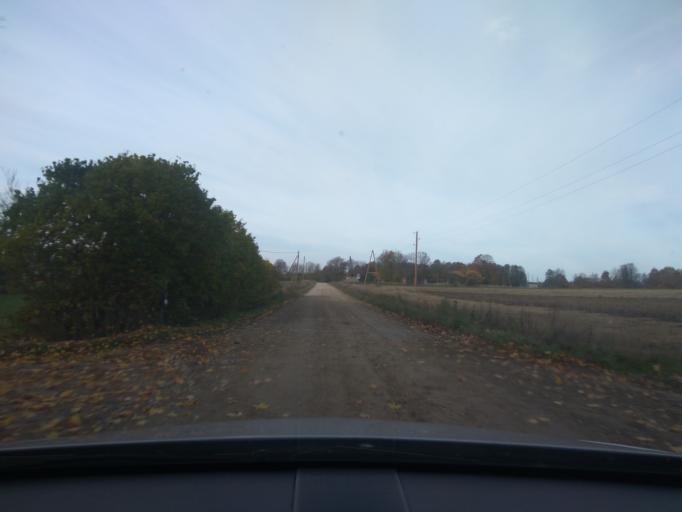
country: LV
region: Alsunga
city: Alsunga
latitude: 56.8746
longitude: 21.6848
